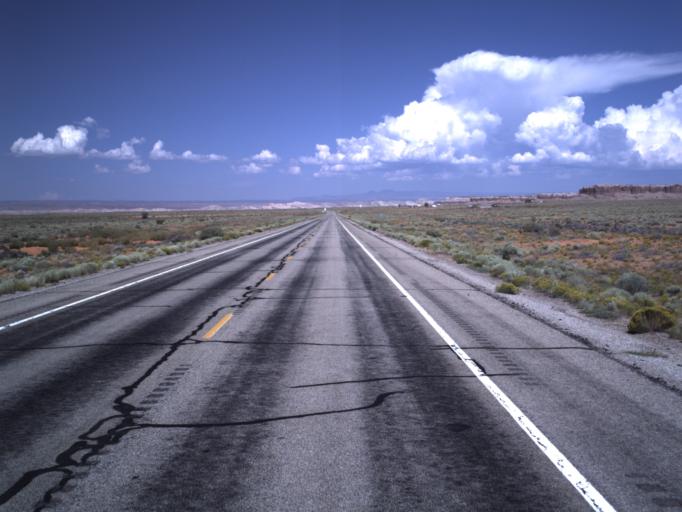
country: US
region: Utah
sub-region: San Juan County
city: Blanding
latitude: 37.1607
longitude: -109.5732
